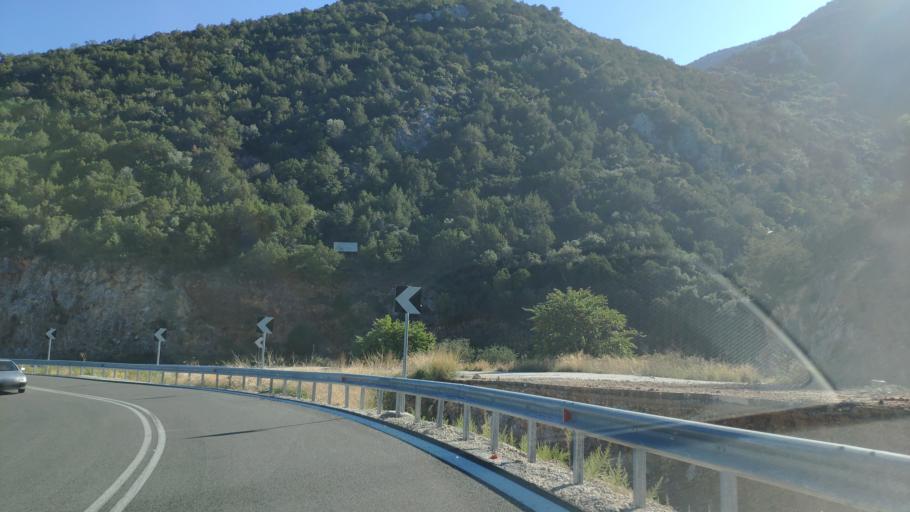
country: GR
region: Peloponnese
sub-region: Nomos Argolidos
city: Didyma
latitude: 37.5530
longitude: 23.2728
